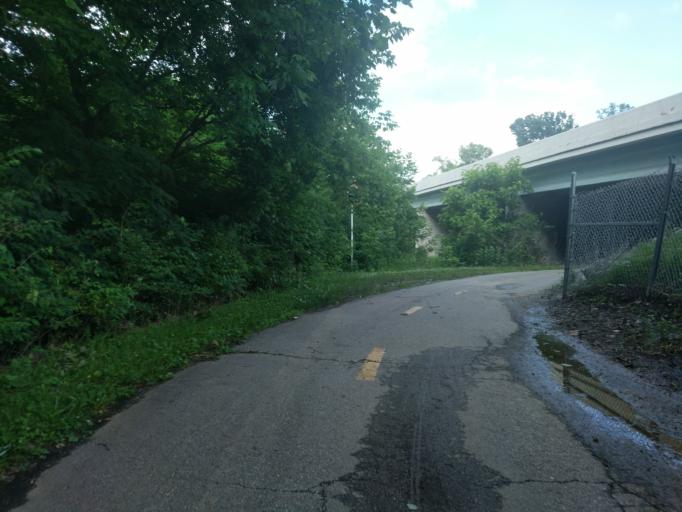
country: US
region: Ohio
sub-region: Franklin County
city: Huber Ridge
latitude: 40.0816
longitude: -82.9201
